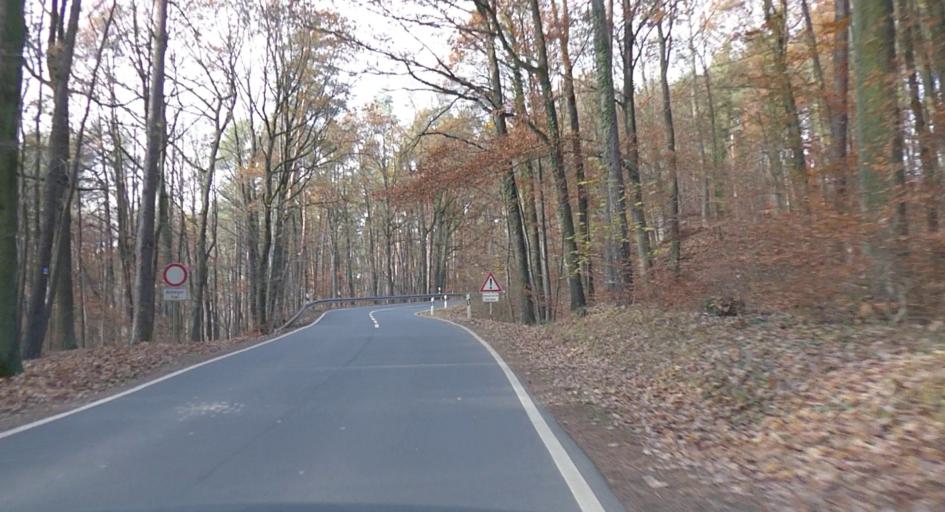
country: DE
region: Bavaria
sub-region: Regierungsbezirk Mittelfranken
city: Bubenreuth
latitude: 49.6160
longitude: 11.0213
